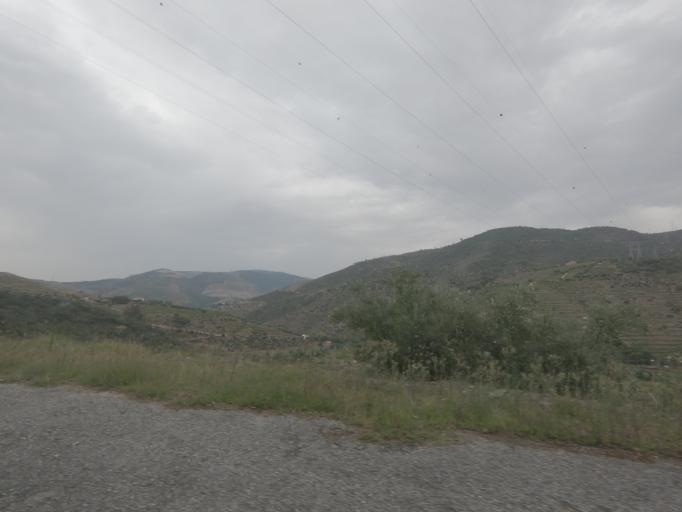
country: PT
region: Viseu
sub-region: Armamar
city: Armamar
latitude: 41.1407
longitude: -7.6437
